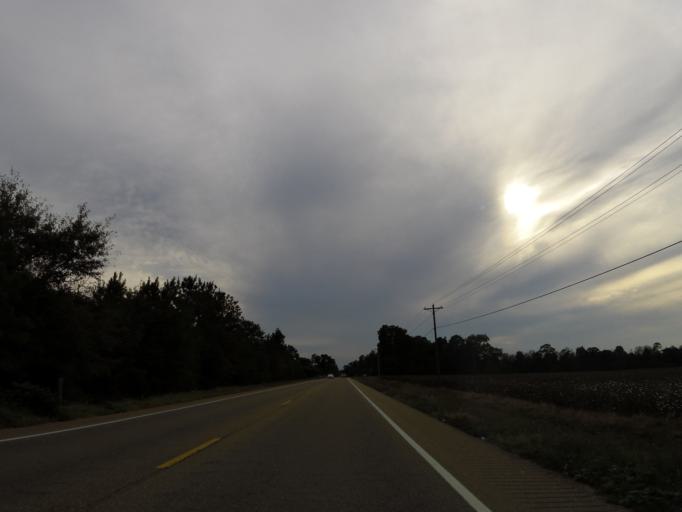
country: US
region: Alabama
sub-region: Monroe County
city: Frisco City
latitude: 31.4484
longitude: -87.3800
